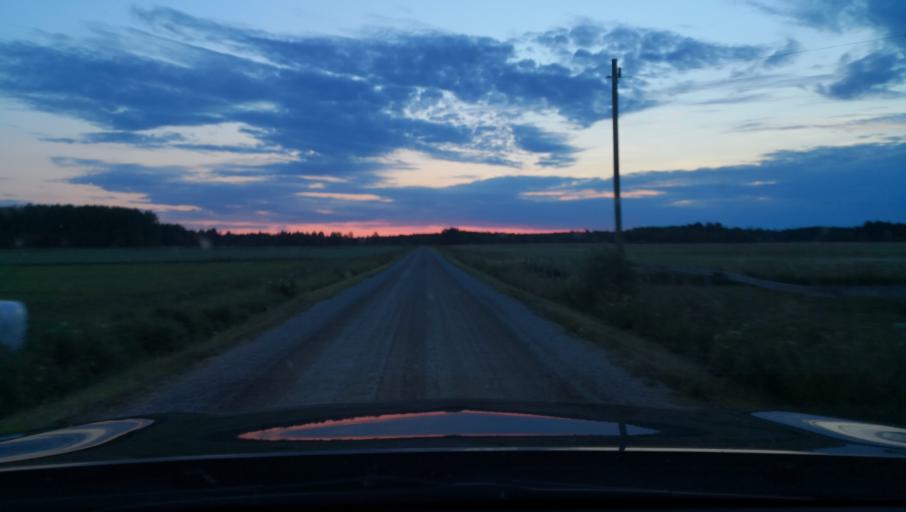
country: SE
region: Uppsala
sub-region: Osthammars Kommun
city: Bjorklinge
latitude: 60.0082
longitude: 17.3289
